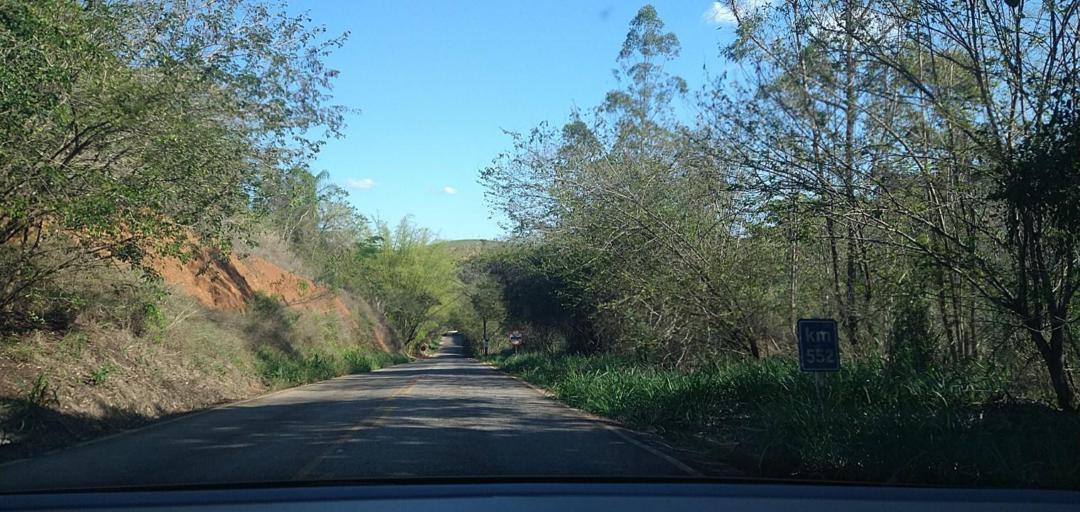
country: BR
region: Minas Gerais
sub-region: Ponte Nova
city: Ponte Nova
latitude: -20.2433
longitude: -42.8944
